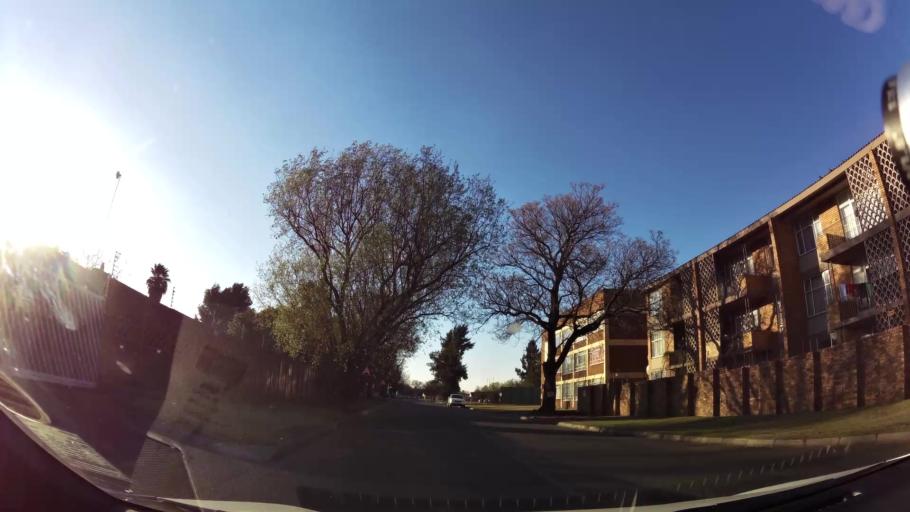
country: ZA
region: Gauteng
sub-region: Ekurhuleni Metropolitan Municipality
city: Germiston
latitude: -26.2867
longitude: 28.1147
